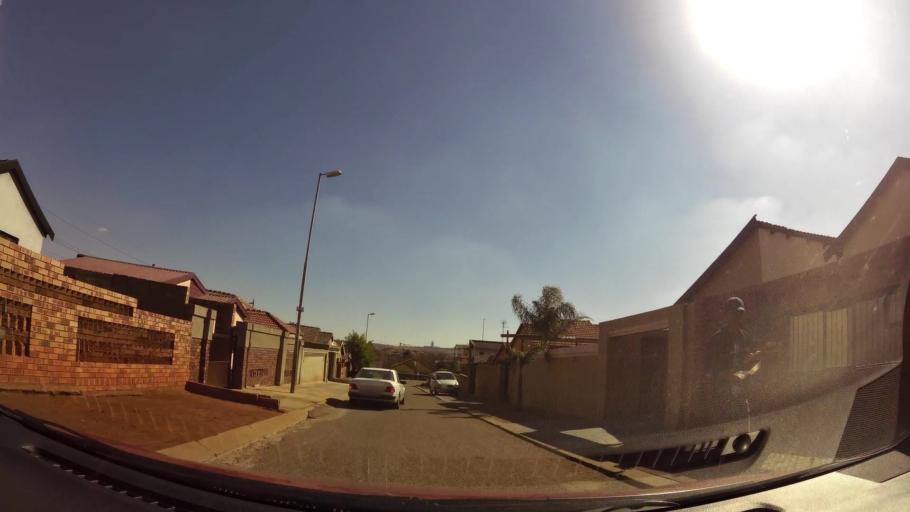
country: ZA
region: Gauteng
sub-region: City of Johannesburg Metropolitan Municipality
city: Soweto
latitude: -26.2355
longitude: 27.8202
